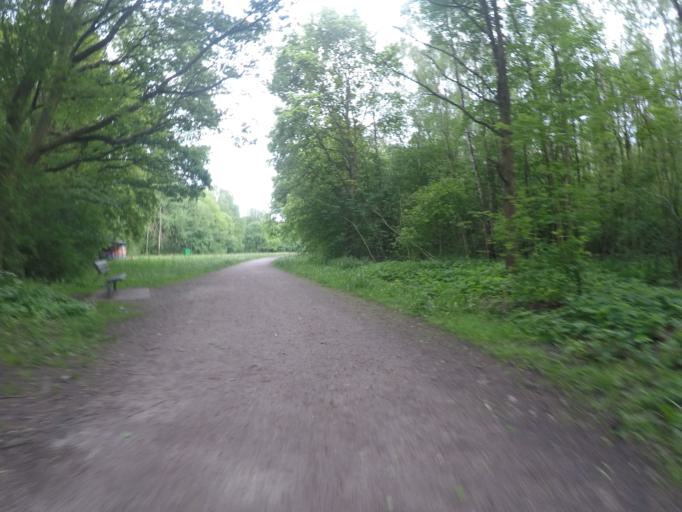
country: DE
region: Schleswig-Holstein
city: Bonningstedt
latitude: 53.6476
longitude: 9.9468
